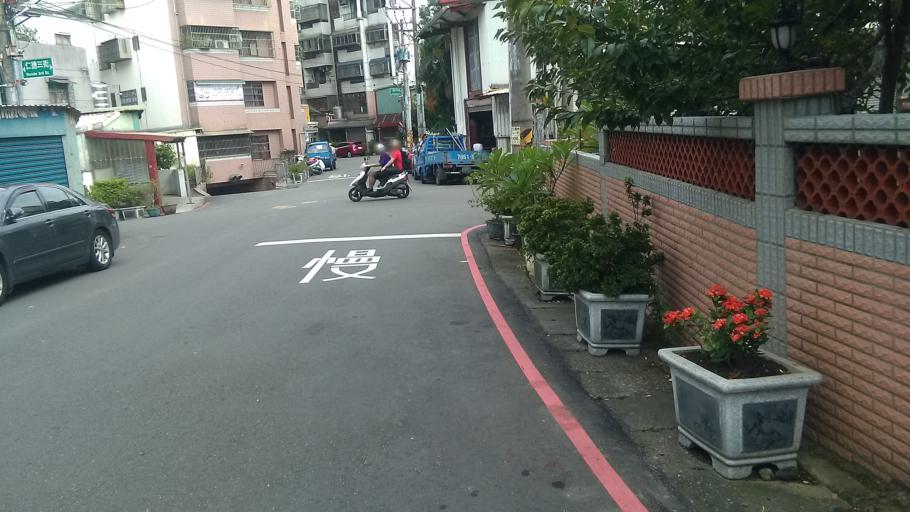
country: TW
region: Taiwan
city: Taoyuan City
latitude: 24.9526
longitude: 121.2626
